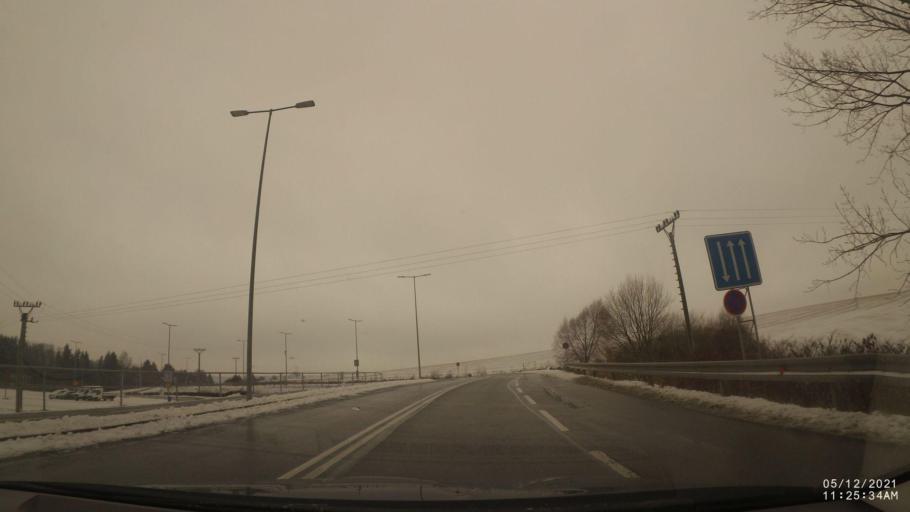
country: CZ
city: Kvasiny
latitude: 50.2001
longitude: 16.2550
